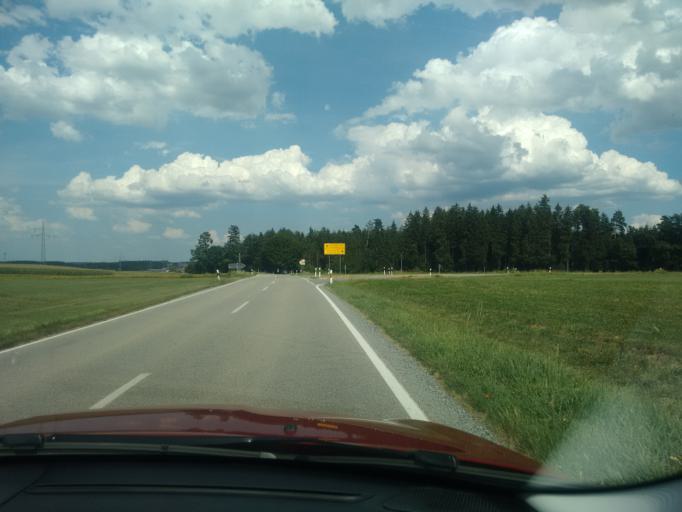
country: DE
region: Bavaria
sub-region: Upper Bavaria
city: Tacherting
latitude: 48.0555
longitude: 12.5995
